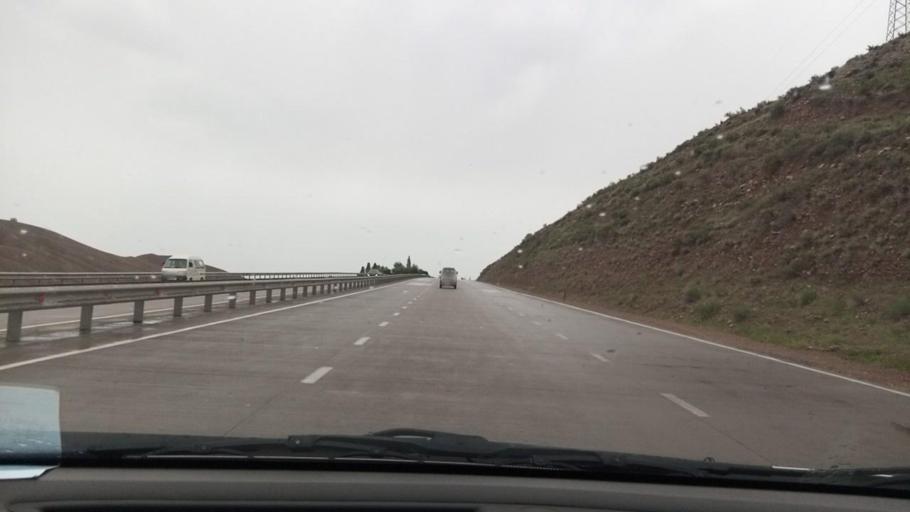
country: UZ
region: Namangan
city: Pop Shahri
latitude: 40.9441
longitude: 70.6856
